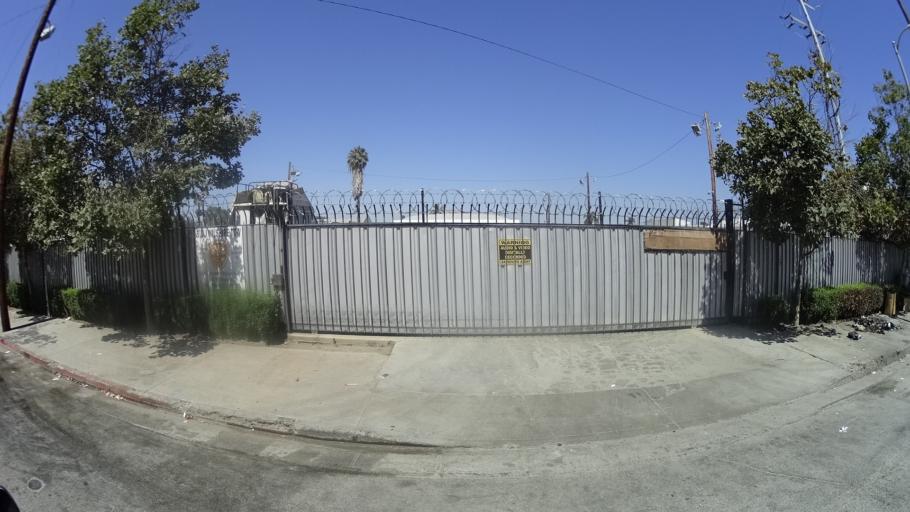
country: US
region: California
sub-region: Los Angeles County
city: View Park-Windsor Hills
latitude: 33.9826
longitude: -118.3116
